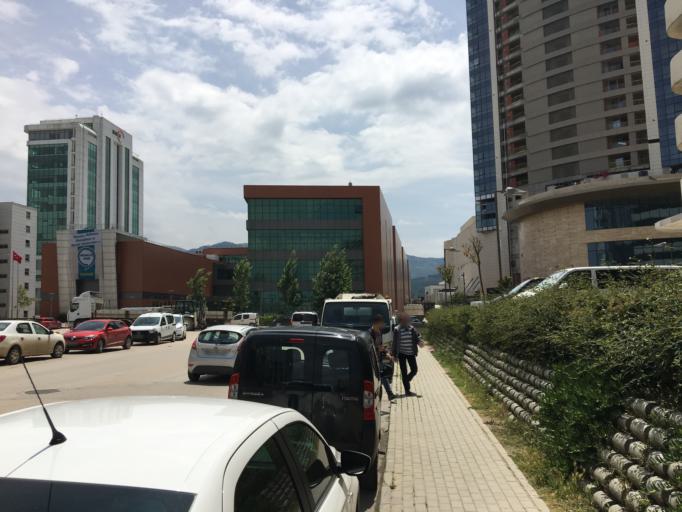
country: TR
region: Bursa
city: Yildirim
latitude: 40.2087
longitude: 28.9973
